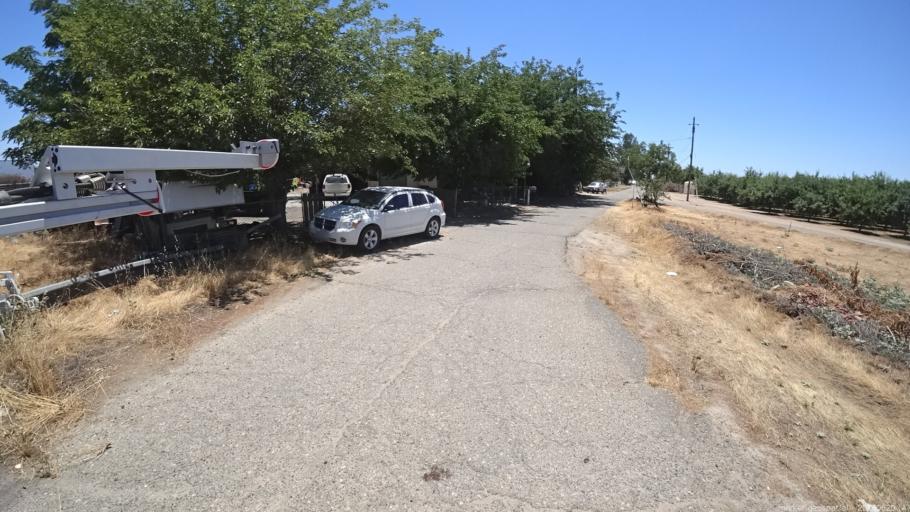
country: US
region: California
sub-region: Fresno County
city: Biola
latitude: 36.8695
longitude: -119.9651
